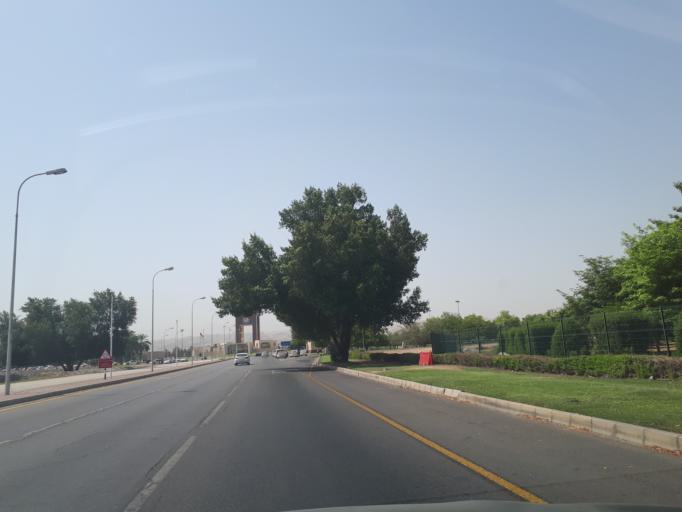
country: OM
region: Muhafazat Masqat
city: As Sib al Jadidah
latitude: 23.5904
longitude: 58.2513
